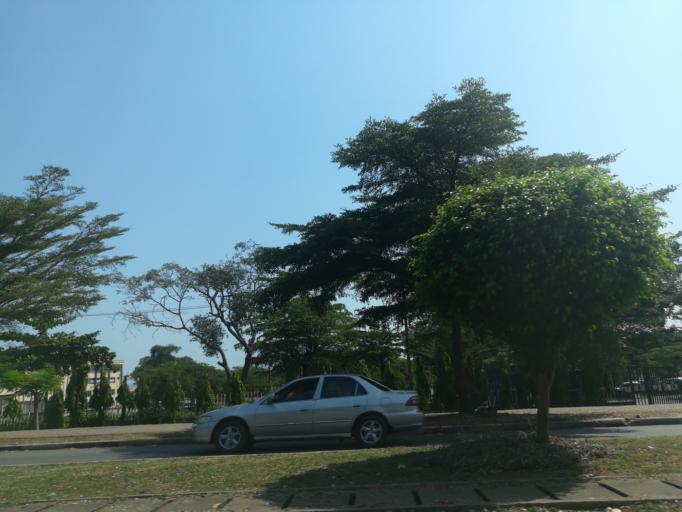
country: NG
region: Abuja Federal Capital Territory
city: Abuja
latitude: 9.0618
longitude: 7.4563
